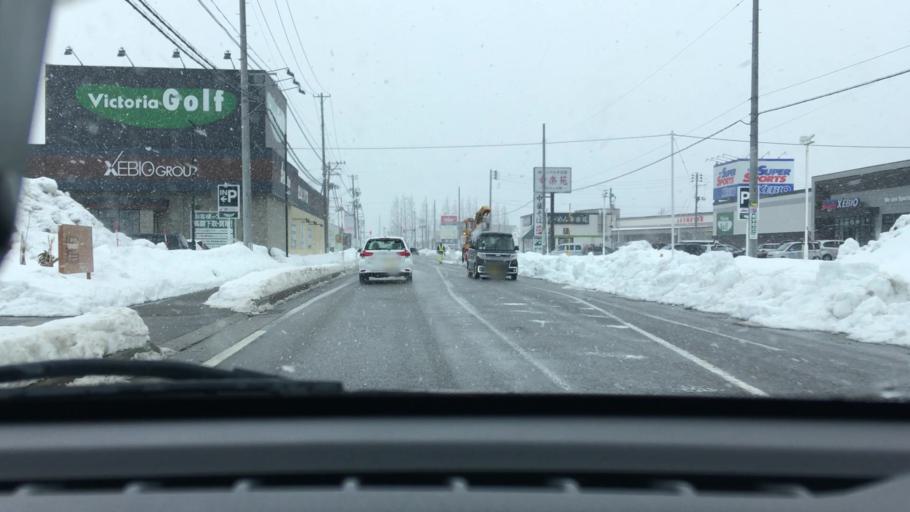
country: JP
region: Niigata
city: Joetsu
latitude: 37.1601
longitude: 138.2534
